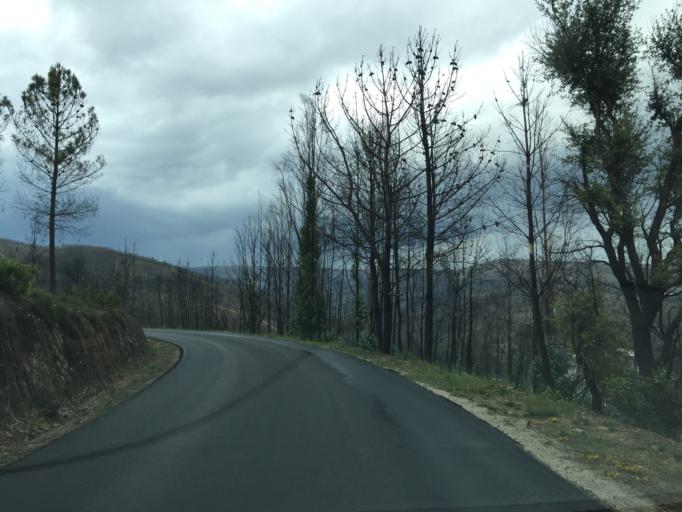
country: PT
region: Coimbra
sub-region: Pampilhosa da Serra
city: Pampilhosa da Serra
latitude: 40.0576
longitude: -8.0076
